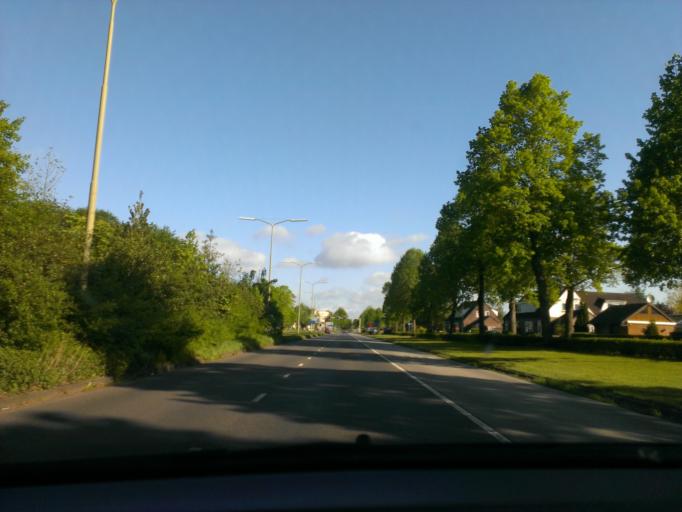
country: NL
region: Drenthe
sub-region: Gemeente Emmen
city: Emmen
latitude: 52.7736
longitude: 6.8944
